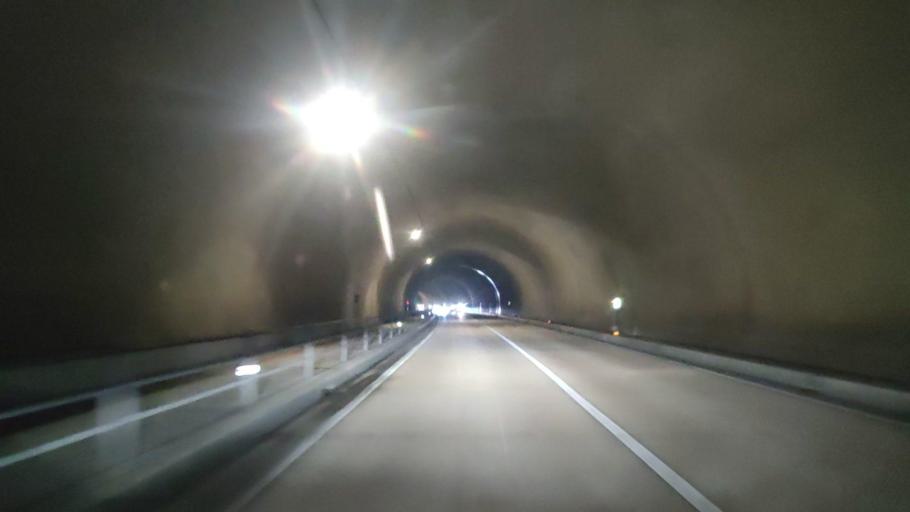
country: JP
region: Gifu
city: Godo
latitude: 35.5895
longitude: 136.6302
